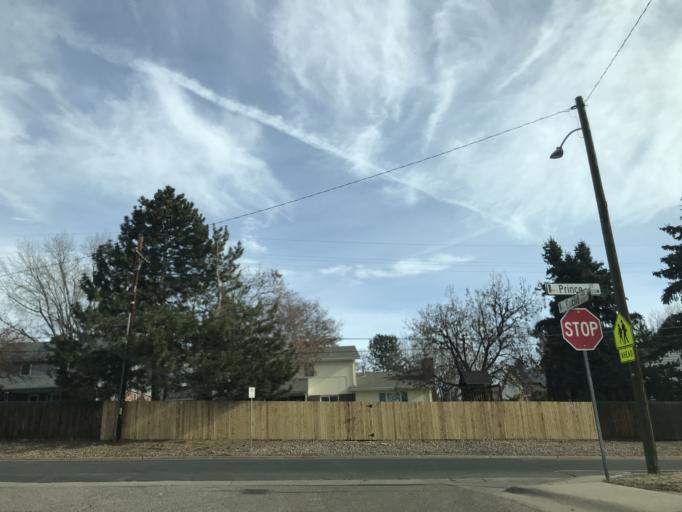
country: US
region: Colorado
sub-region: Arapahoe County
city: Littleton
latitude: 39.5978
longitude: -105.0166
